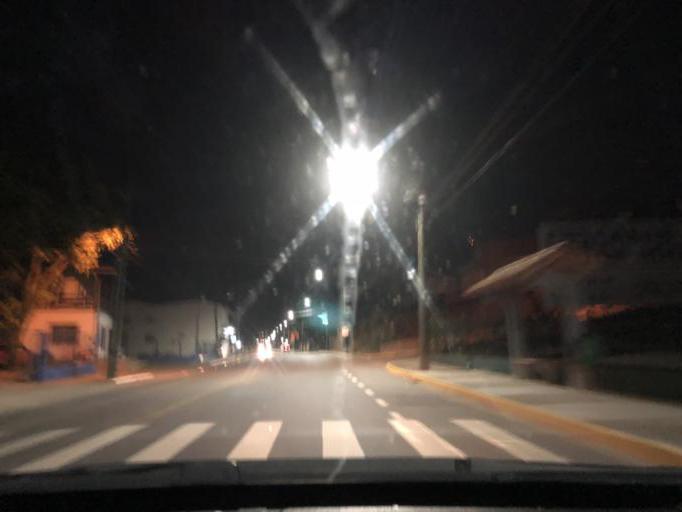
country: BR
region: Santa Catarina
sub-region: Jaragua Do Sul
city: Jaragua do Sul
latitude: -26.5077
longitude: -49.1022
